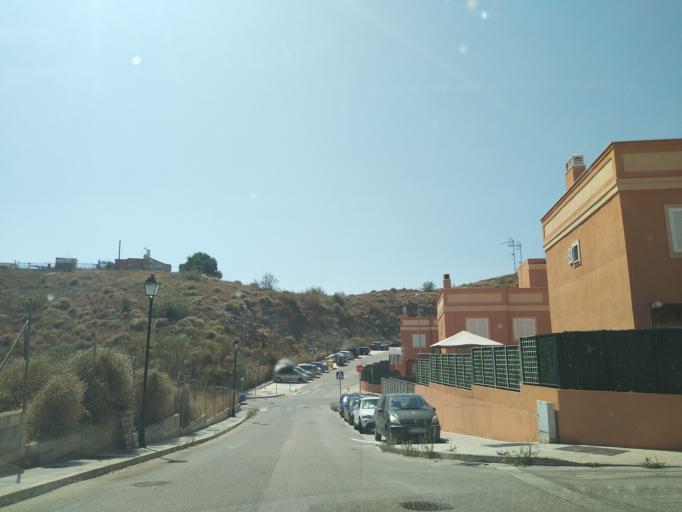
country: ES
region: Andalusia
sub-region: Provincia de Malaga
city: Valdes
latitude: 36.7196
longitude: -4.1988
